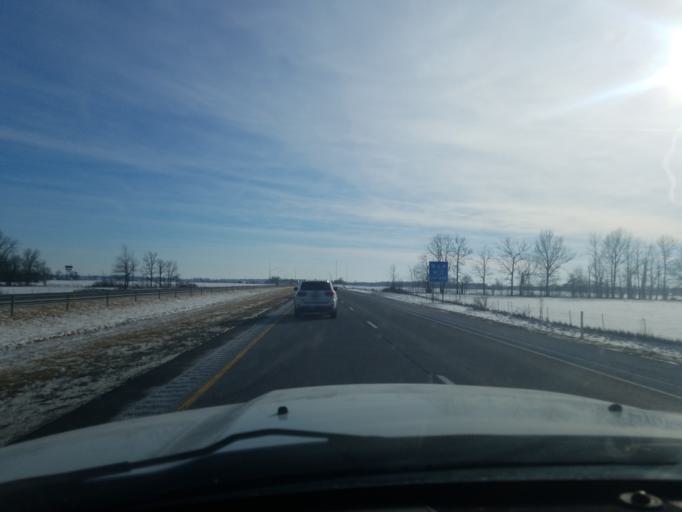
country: US
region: Indiana
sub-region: Madison County
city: Alexandria
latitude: 40.2855
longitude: -85.5582
